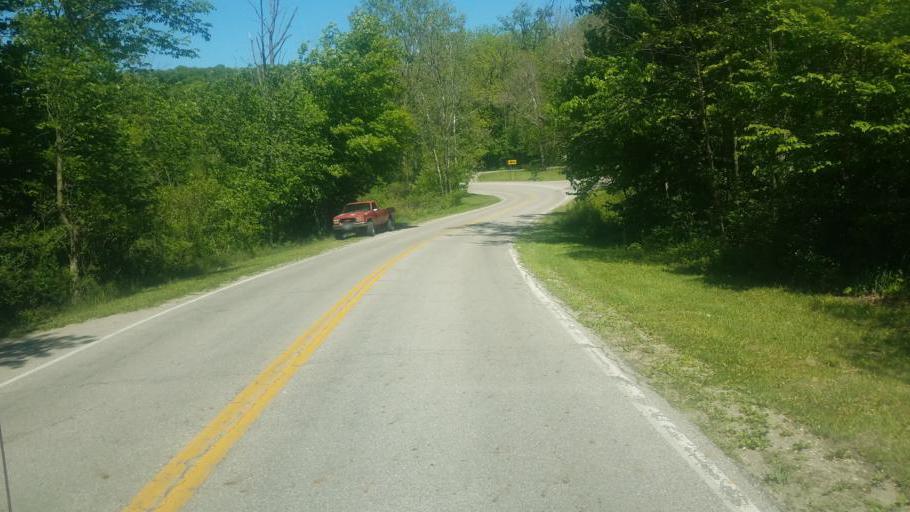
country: US
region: Ohio
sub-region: Champaign County
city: Saint Paris
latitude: 40.1787
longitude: -83.9507
